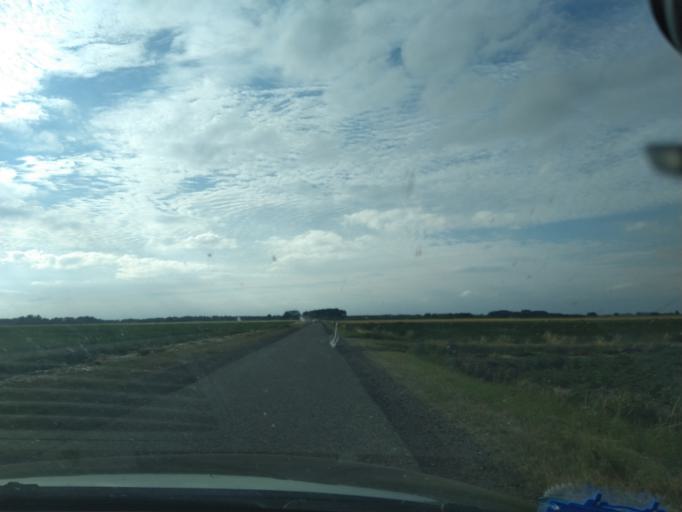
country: NL
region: Groningen
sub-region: Gemeente Vlagtwedde
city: Vlagtwedde
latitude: 53.0810
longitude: 7.1112
